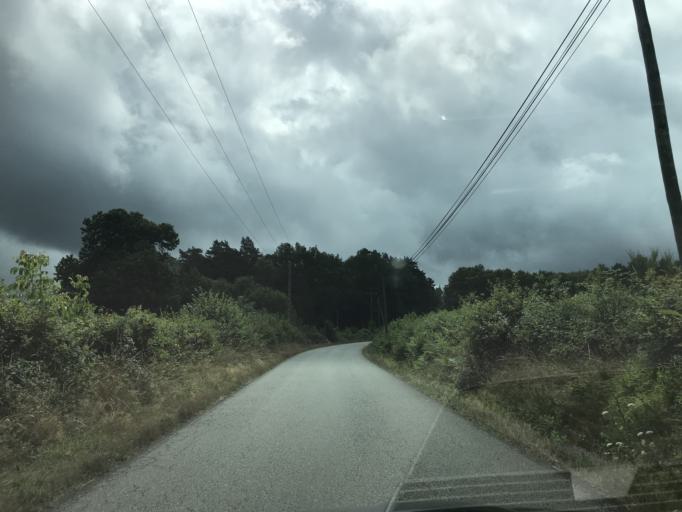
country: FR
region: Auvergne
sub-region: Departement du Cantal
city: Pleaux
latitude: 45.2504
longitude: 2.1961
